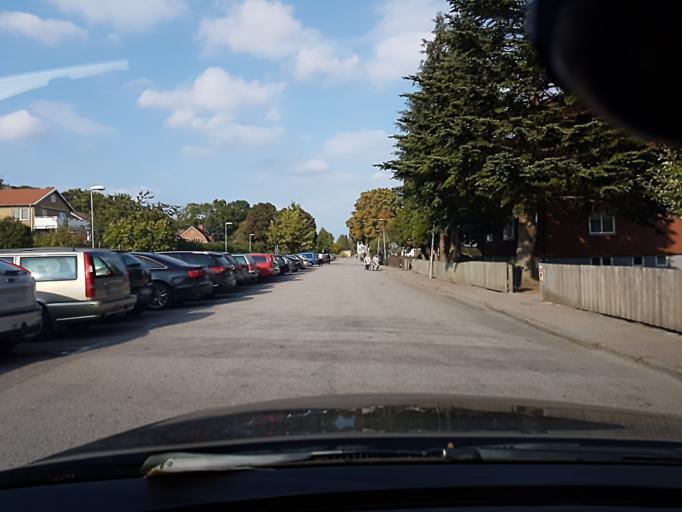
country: SE
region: Kronoberg
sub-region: Vaxjo Kommun
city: Vaexjoe
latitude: 56.8804
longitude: 14.7977
